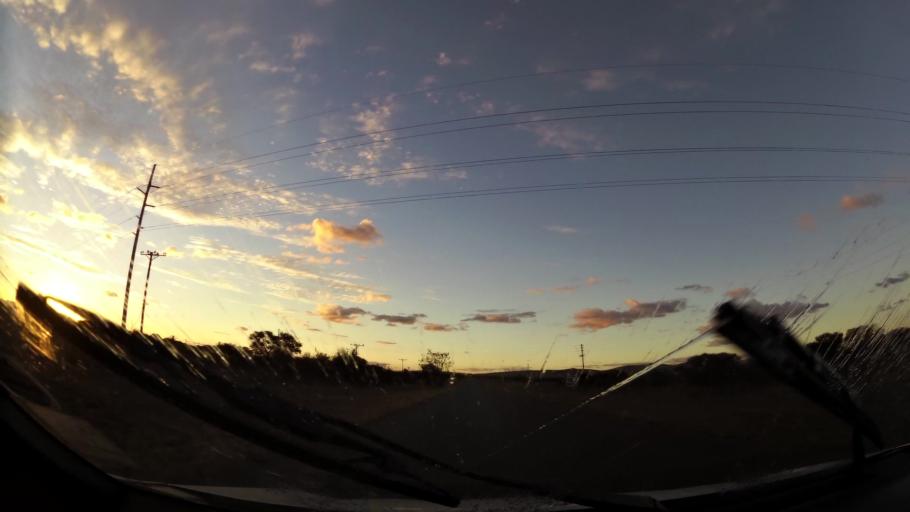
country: ZA
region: Limpopo
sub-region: Capricorn District Municipality
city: Polokwane
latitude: -23.7494
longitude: 29.4716
